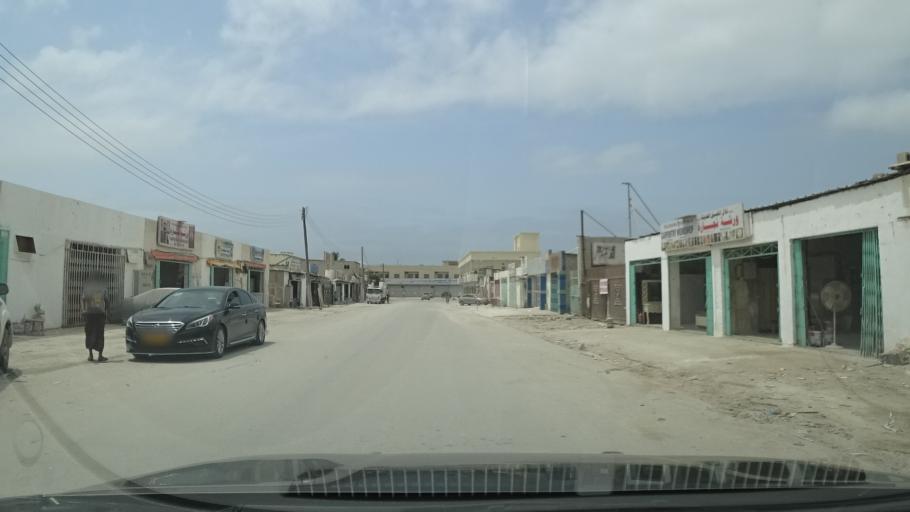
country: OM
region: Zufar
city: Salalah
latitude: 17.0217
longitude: 54.0486
